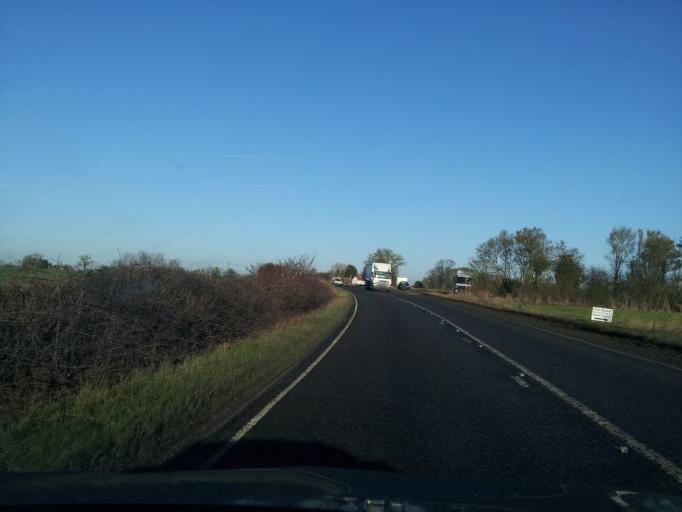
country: GB
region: England
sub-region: Suffolk
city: Lavenham
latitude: 52.1185
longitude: 0.7509
